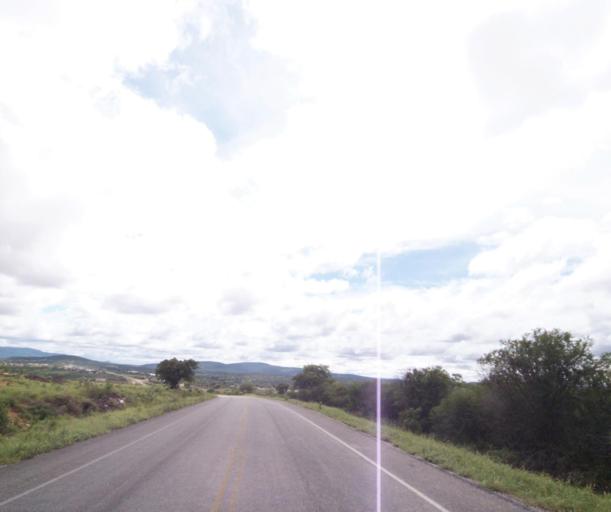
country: BR
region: Bahia
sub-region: Brumado
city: Brumado
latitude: -14.2364
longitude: -41.6917
